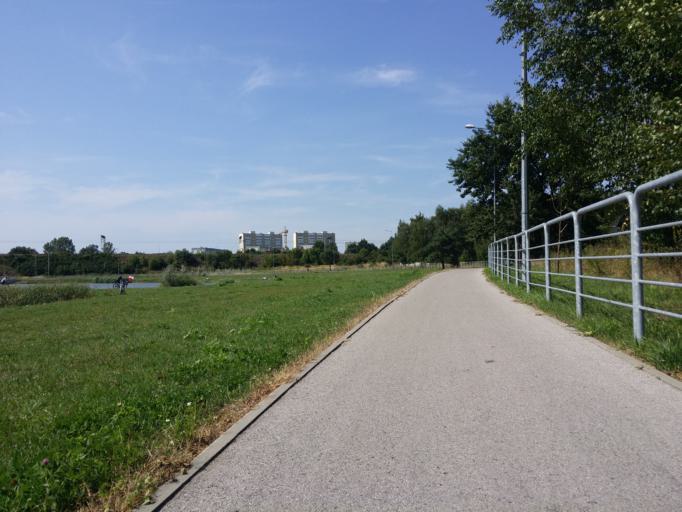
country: PL
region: Masovian Voivodeship
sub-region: Powiat radomski
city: Trablice
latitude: 51.3684
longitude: 21.1434
